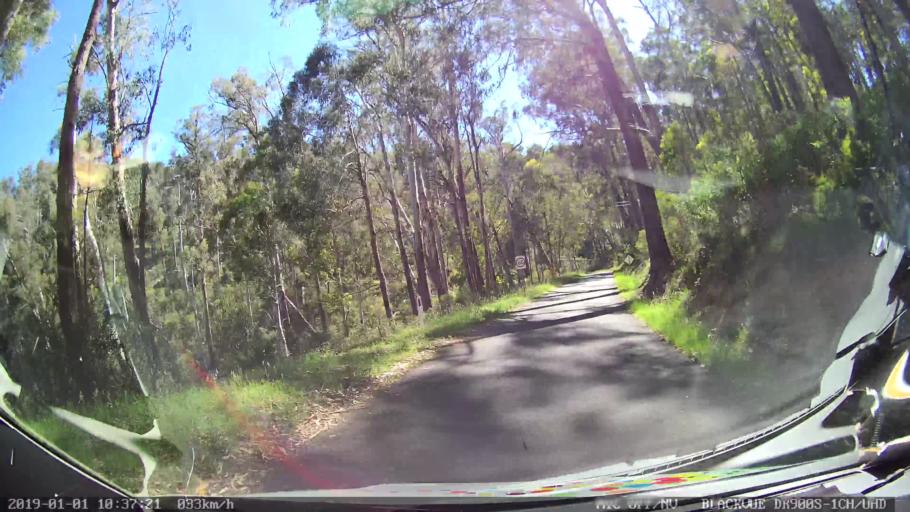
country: AU
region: New South Wales
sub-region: Snowy River
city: Jindabyne
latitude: -36.0491
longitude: 148.3037
